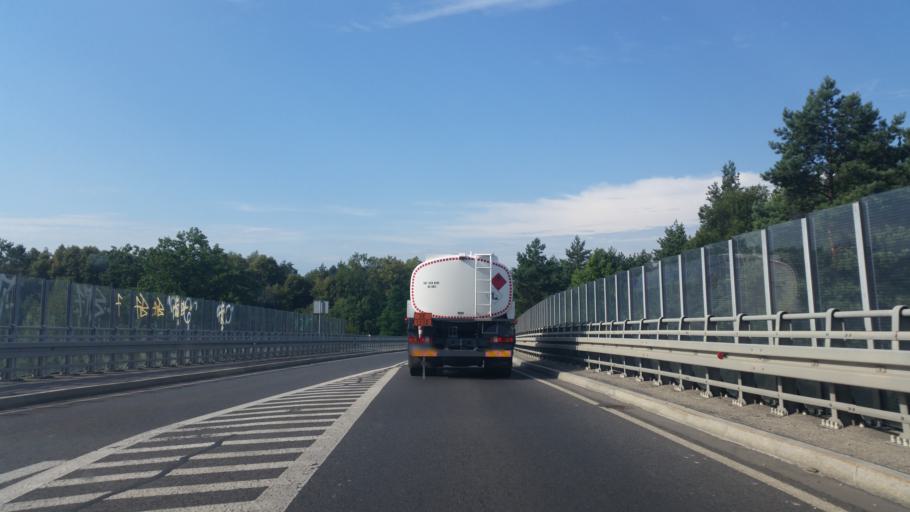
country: PL
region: Lesser Poland Voivodeship
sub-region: Powiat chrzanowski
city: Chrzanow
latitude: 50.1235
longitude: 19.3654
